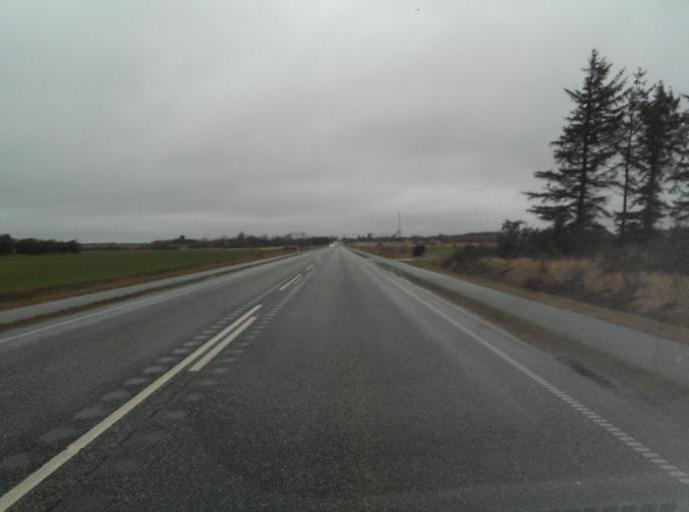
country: DK
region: Central Jutland
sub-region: Ringkobing-Skjern Kommune
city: Ringkobing
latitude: 56.1303
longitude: 8.2806
